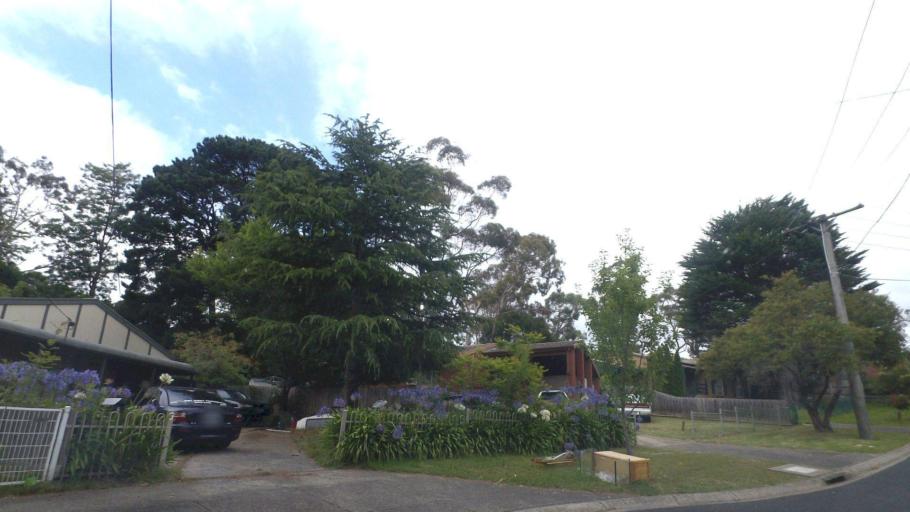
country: AU
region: Victoria
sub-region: Knox
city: The Basin
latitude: -37.8551
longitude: 145.3110
